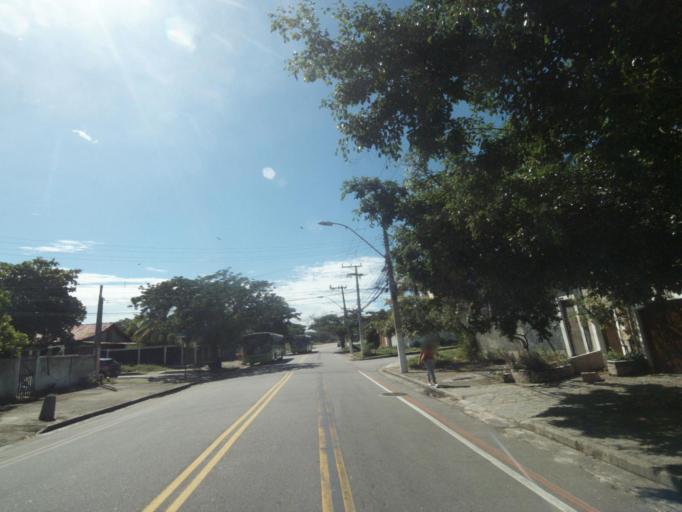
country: BR
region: Rio de Janeiro
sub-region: Niteroi
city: Niteroi
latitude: -22.9530
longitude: -43.0799
